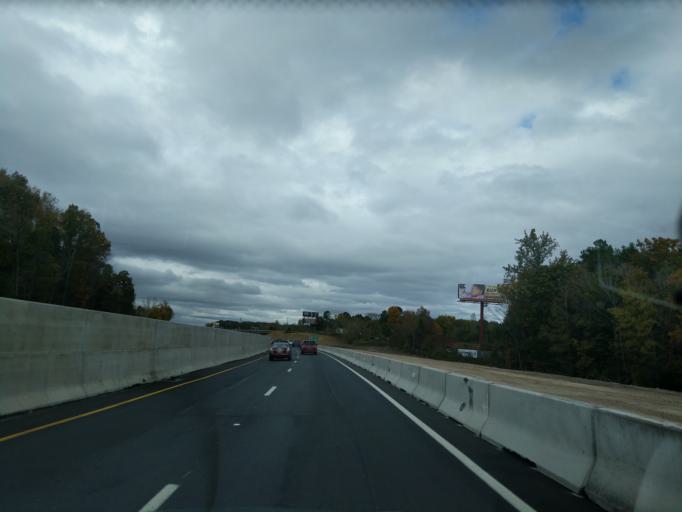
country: US
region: North Carolina
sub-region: Cabarrus County
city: Kannapolis
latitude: 35.5042
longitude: -80.5622
